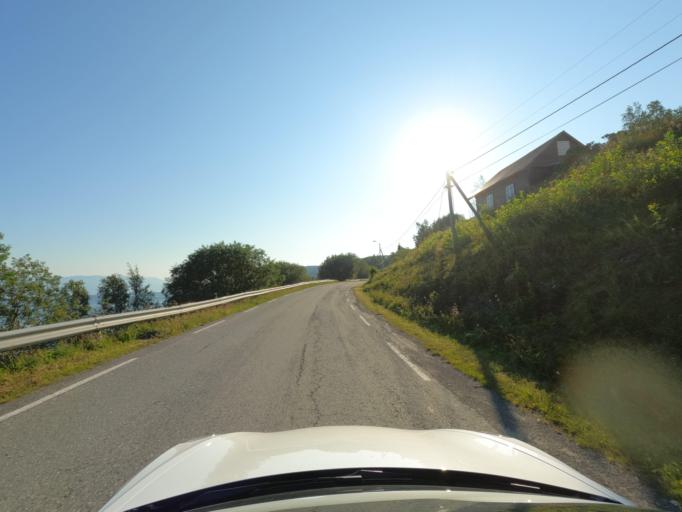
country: NO
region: Nordland
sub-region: Narvik
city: Narvik
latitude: 68.5264
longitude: 17.4523
